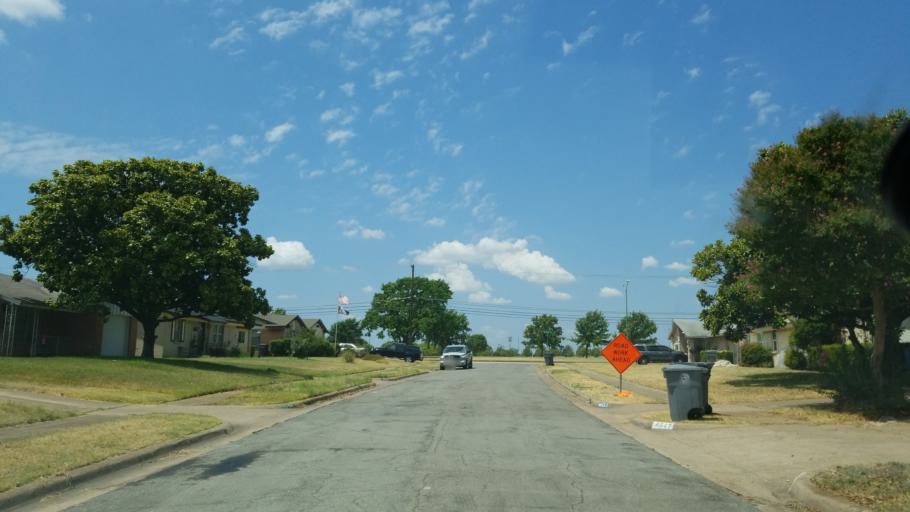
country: US
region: Texas
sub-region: Dallas County
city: Cockrell Hill
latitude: 32.7219
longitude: -96.8992
